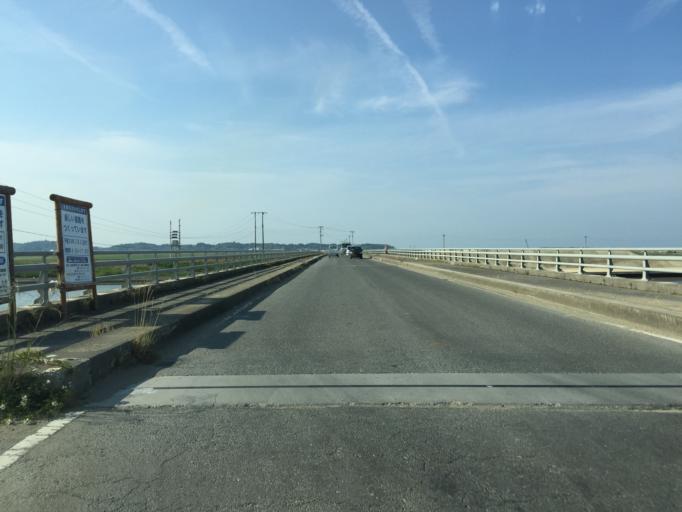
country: JP
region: Fukushima
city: Namie
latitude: 37.6864
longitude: 141.0050
